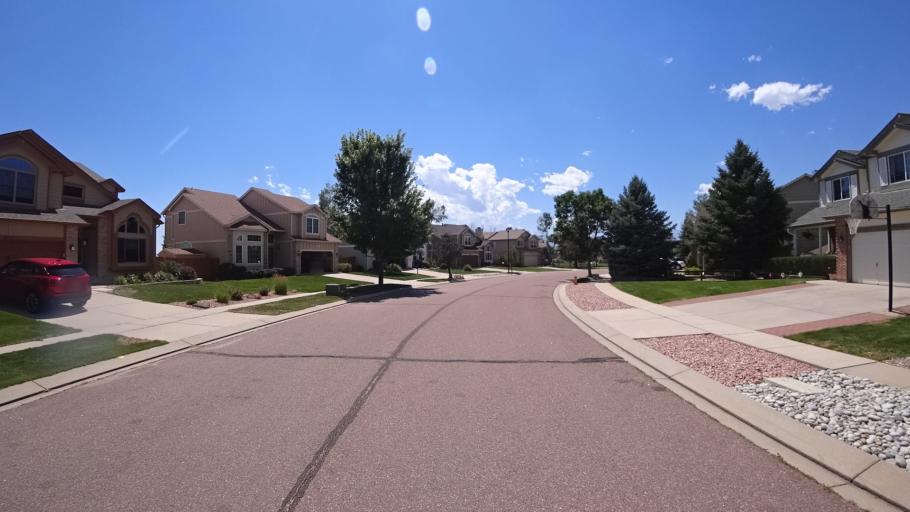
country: US
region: Colorado
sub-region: El Paso County
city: Black Forest
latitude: 38.9523
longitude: -104.7432
